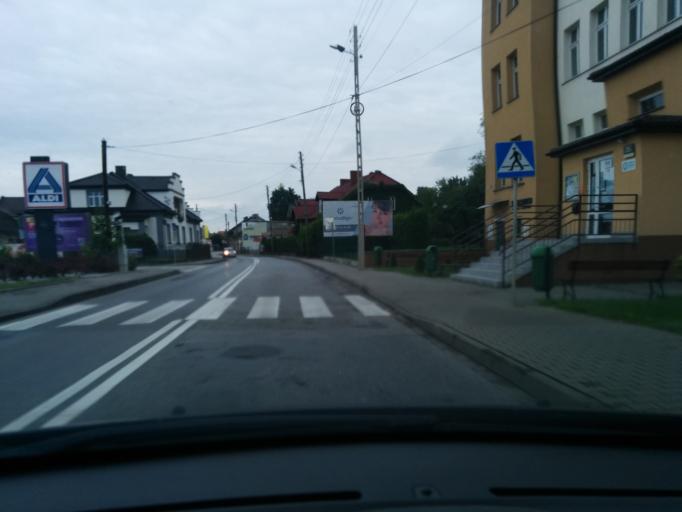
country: PL
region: Lesser Poland Voivodeship
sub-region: Powiat oswiecimski
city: Kety
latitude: 49.8834
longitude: 19.2211
